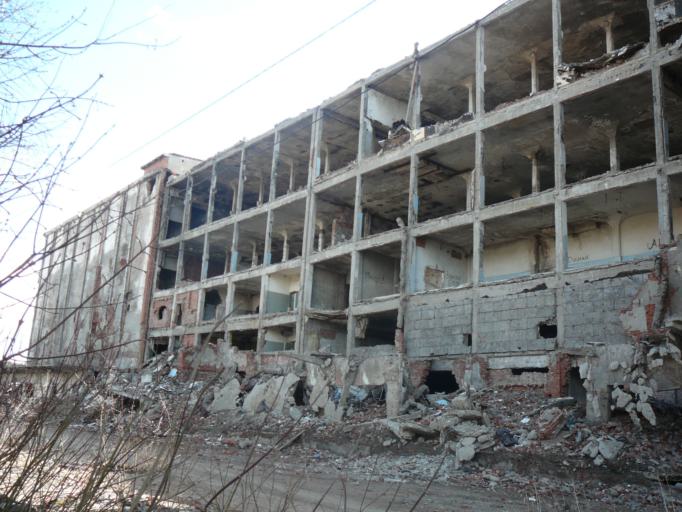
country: RU
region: Saratov
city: Privolzhskiy
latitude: 51.4121
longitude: 46.0517
